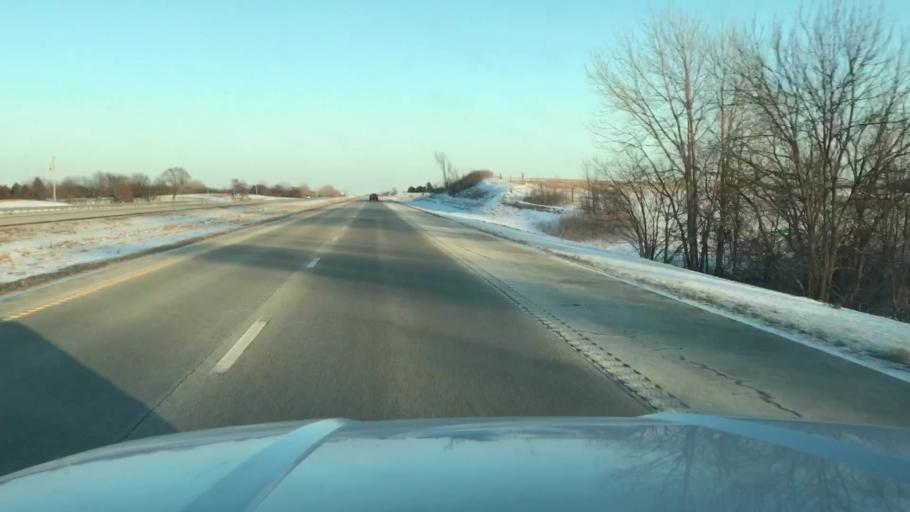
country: US
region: Missouri
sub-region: Clinton County
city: Gower
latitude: 39.7470
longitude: -94.6260
